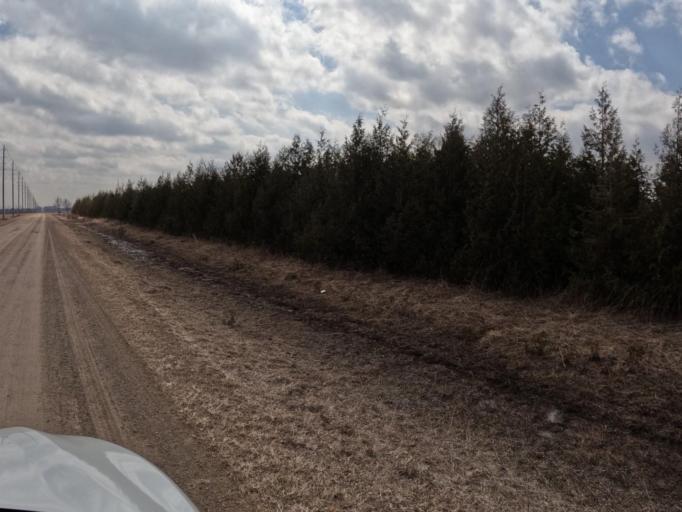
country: CA
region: Ontario
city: Shelburne
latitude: 44.0470
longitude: -80.3191
